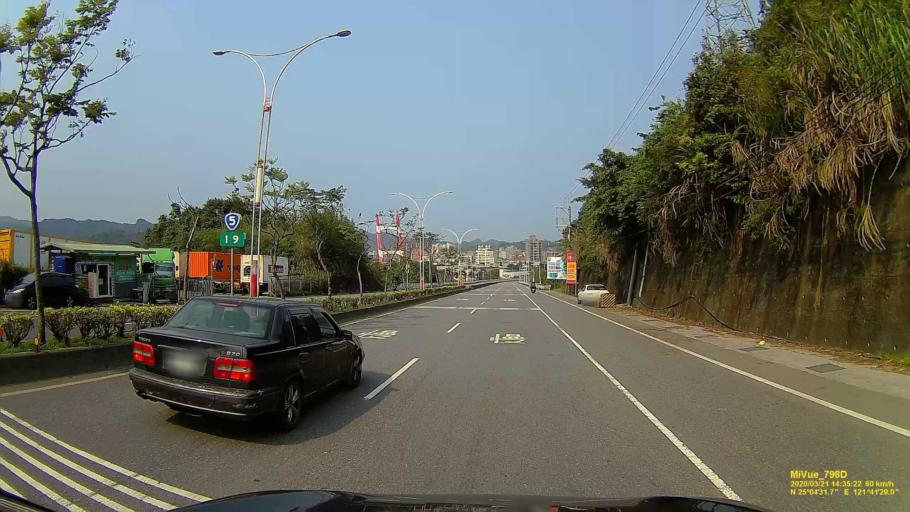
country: TW
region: Taiwan
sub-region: Keelung
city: Keelung
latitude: 25.0755
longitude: 121.6914
